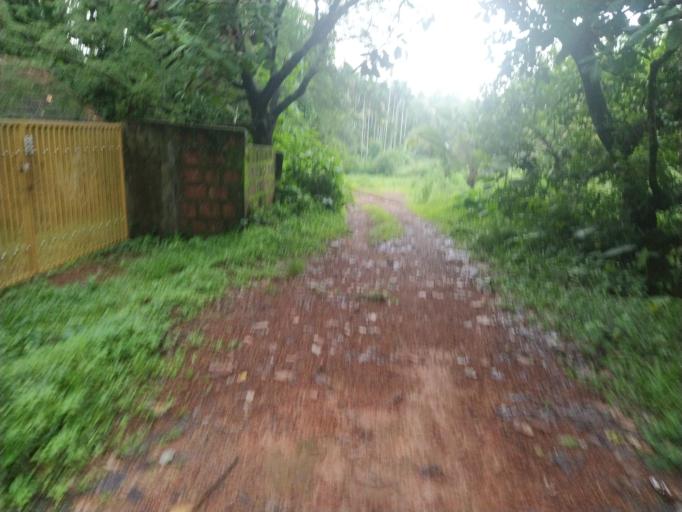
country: IN
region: Kerala
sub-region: Kasaragod District
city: Kannangad
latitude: 12.4041
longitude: 75.0586
